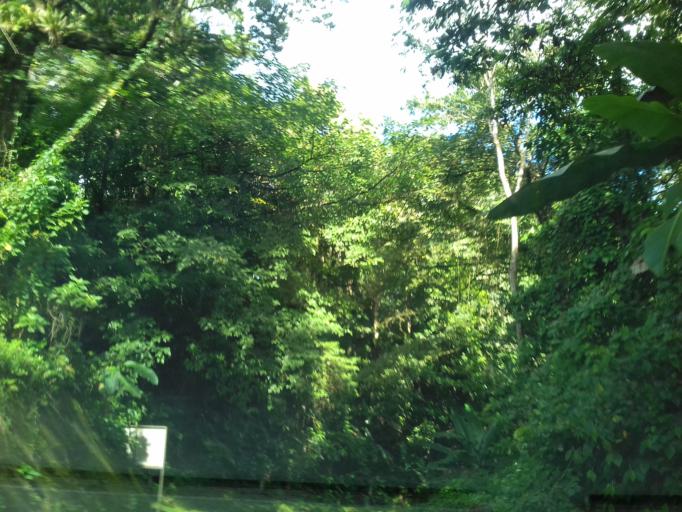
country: MQ
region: Martinique
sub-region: Martinique
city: Saint-Joseph
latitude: 14.6946
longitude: -61.0388
